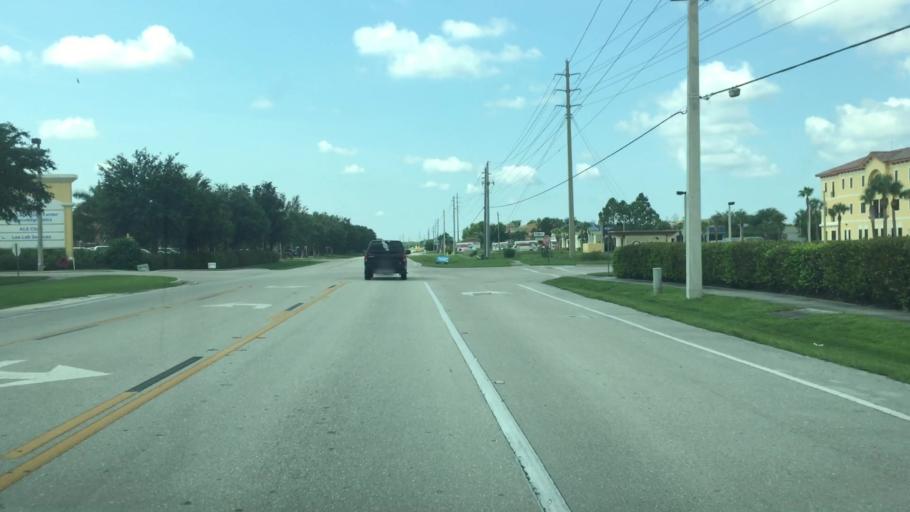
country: US
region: Florida
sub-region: Lee County
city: Villas
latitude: 26.5457
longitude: -81.8469
